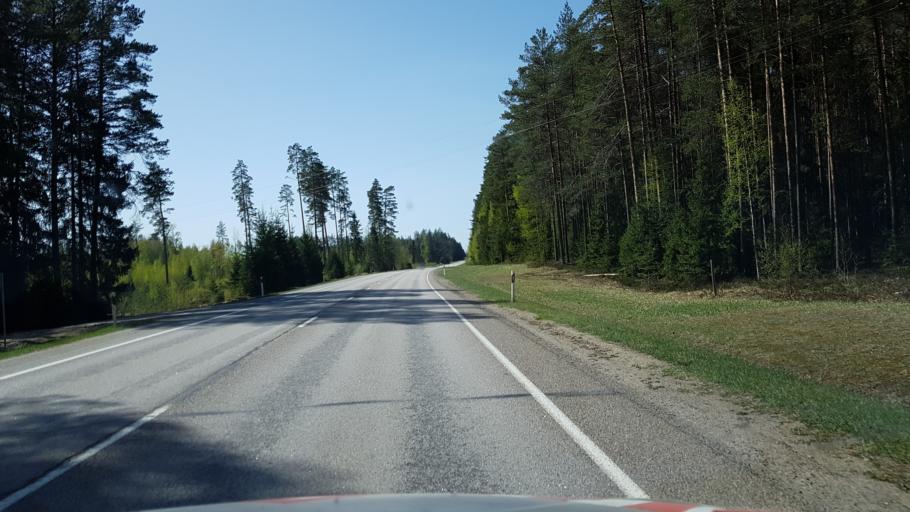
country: EE
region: Valgamaa
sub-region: Valga linn
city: Valga
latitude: 57.8284
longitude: 26.0562
